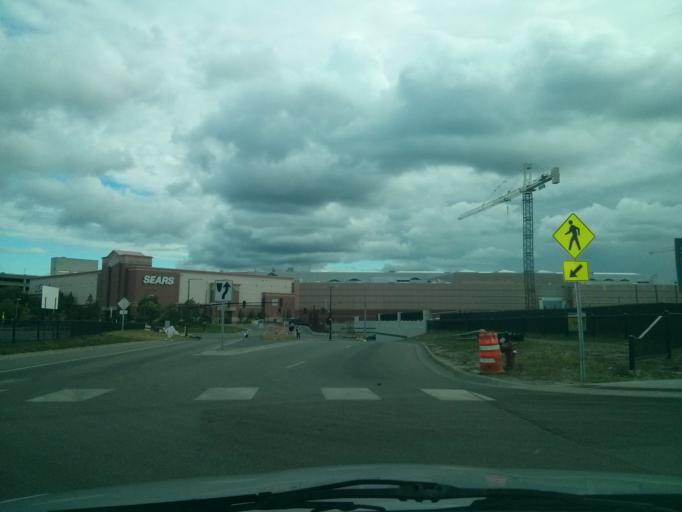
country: US
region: Minnesota
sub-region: Hennepin County
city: Richfield
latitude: 44.8582
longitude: -93.2406
